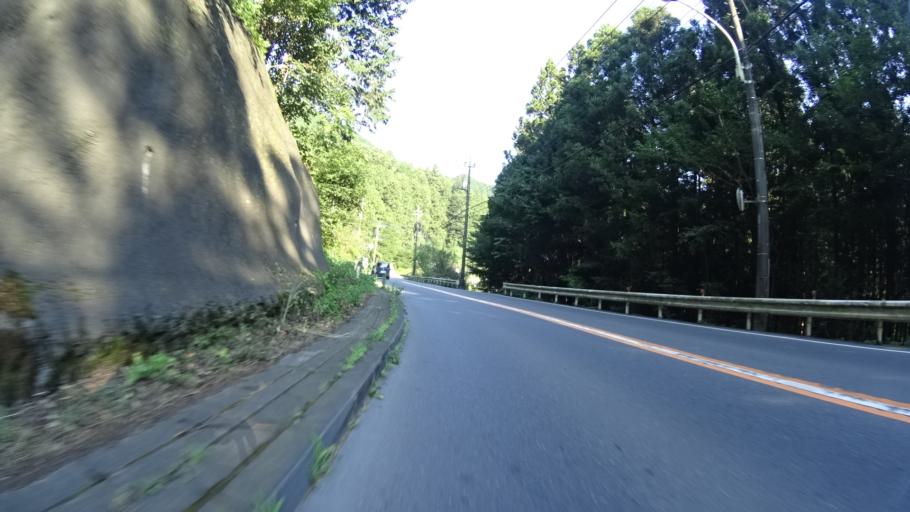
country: JP
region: Tokyo
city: Ome
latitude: 35.8054
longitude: 139.1701
